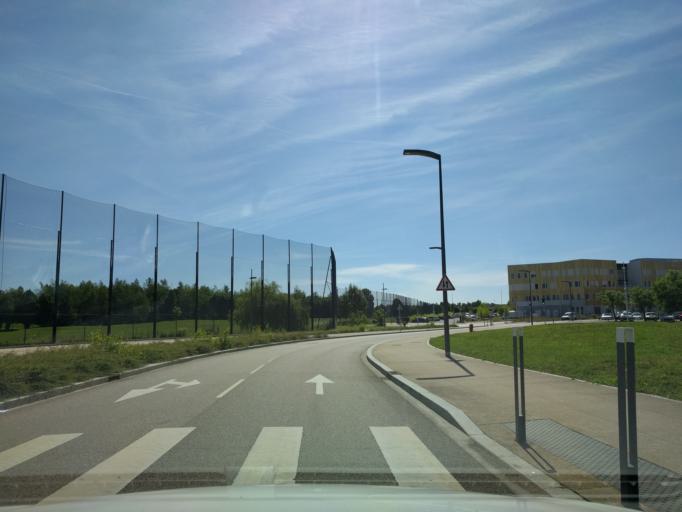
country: FR
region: Lorraine
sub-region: Departement de la Moselle
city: Peltre
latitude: 49.0960
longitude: 6.2280
